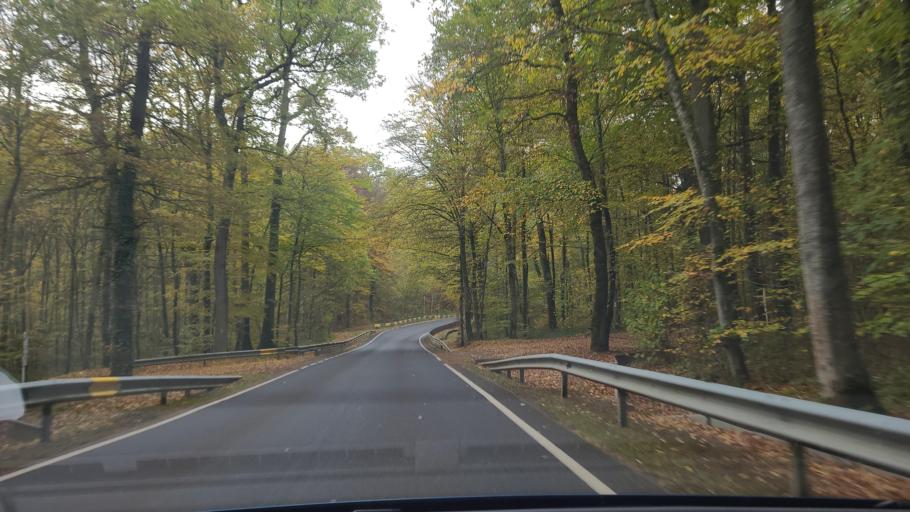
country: LU
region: Luxembourg
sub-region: Canton de Capellen
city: Dippach
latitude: 49.6049
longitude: 6.0004
